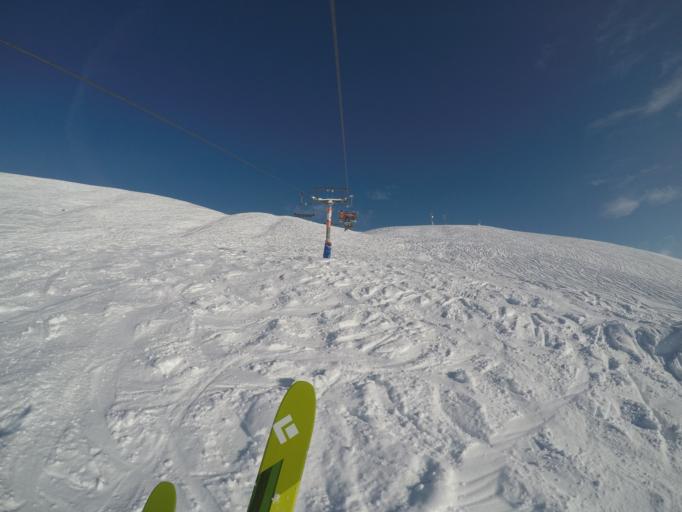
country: GE
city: Gudauri
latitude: 42.4853
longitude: 44.4963
